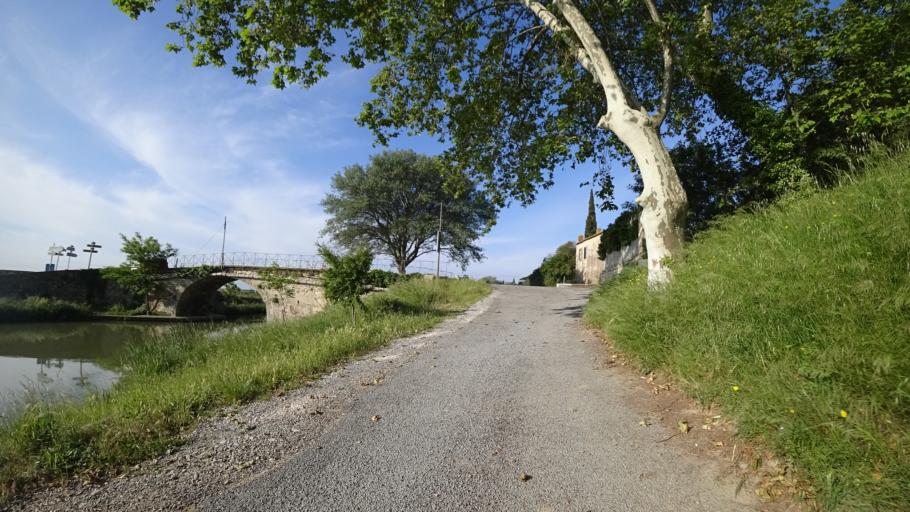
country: FR
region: Languedoc-Roussillon
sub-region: Departement de l'Aude
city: Canet
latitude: 43.2469
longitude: 2.8033
